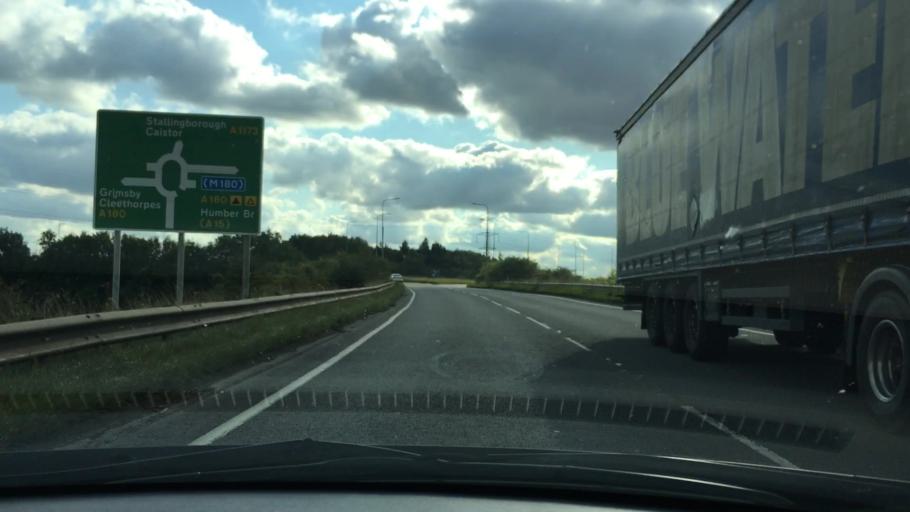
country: GB
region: England
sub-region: North East Lincolnshire
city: Immingham
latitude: 53.5996
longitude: -0.1958
